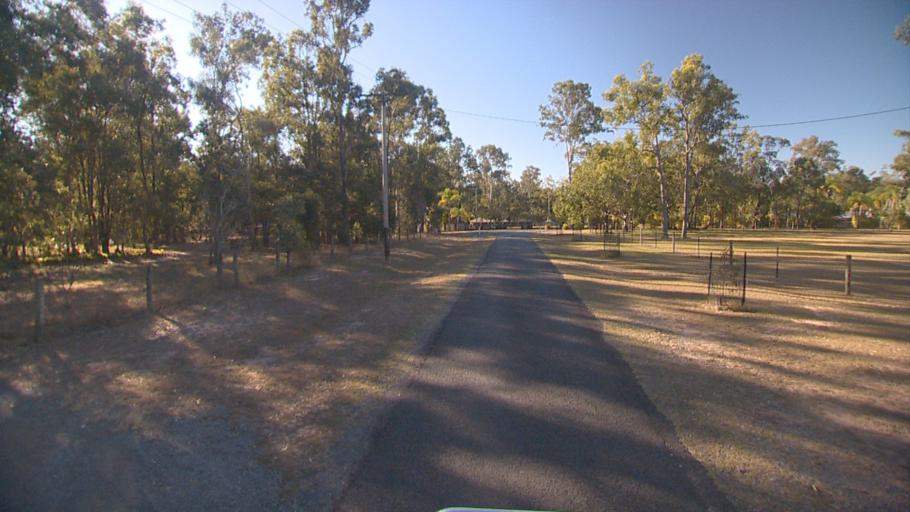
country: AU
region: Queensland
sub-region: Logan
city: North Maclean
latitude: -27.7545
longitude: 153.0097
